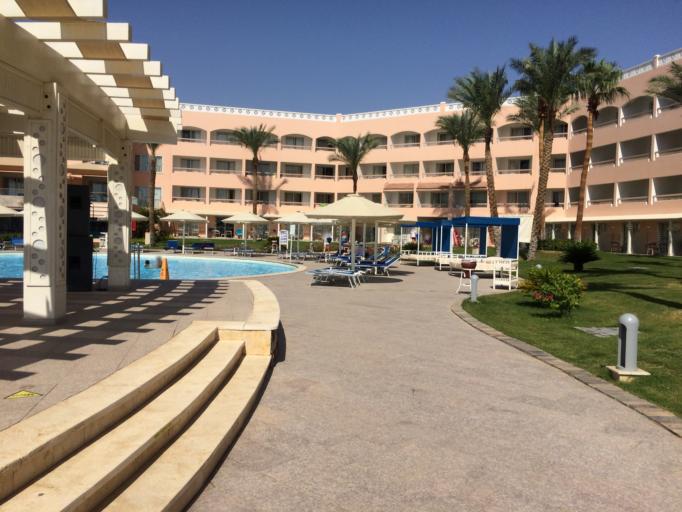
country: EG
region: Red Sea
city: Hurghada
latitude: 27.1227
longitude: 33.8292
